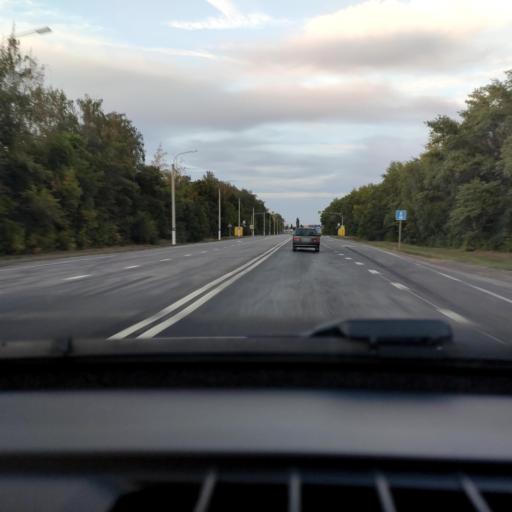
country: RU
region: Voronezj
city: Anna
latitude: 51.5064
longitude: 40.2689
